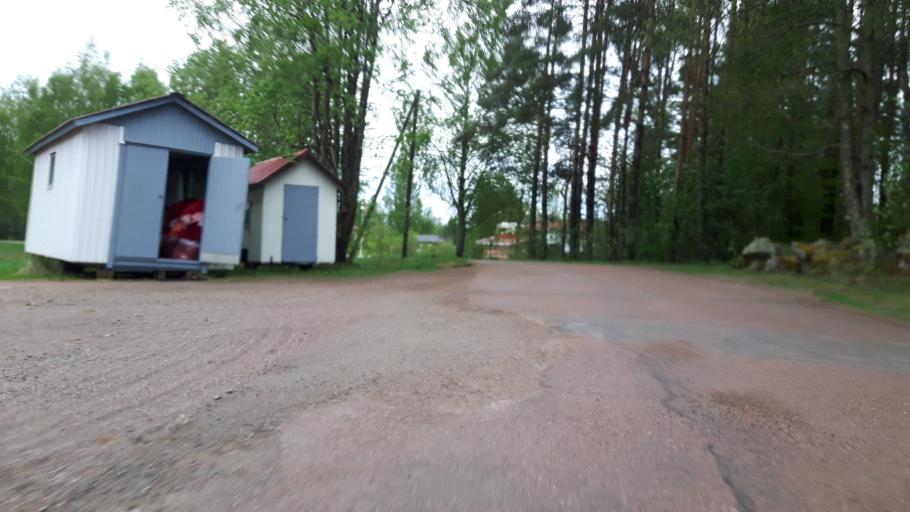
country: FI
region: Kymenlaakso
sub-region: Kotka-Hamina
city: Karhula
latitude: 60.5619
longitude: 27.0441
